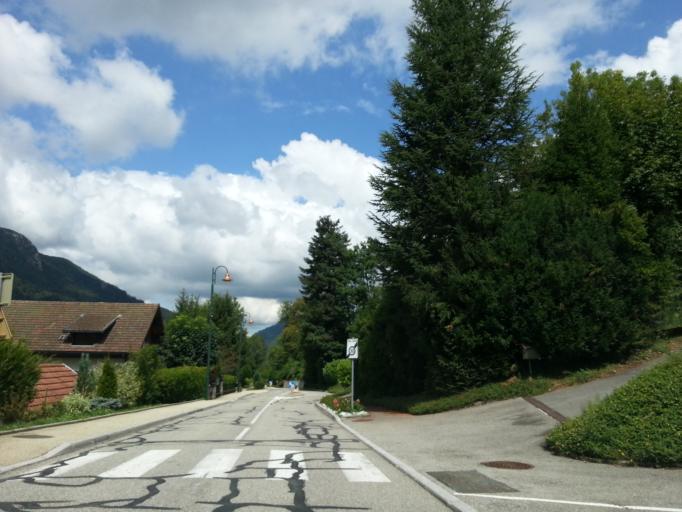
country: FR
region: Rhone-Alpes
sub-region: Departement de la Haute-Savoie
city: Menthon-Saint-Bernard
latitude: 45.8692
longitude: 6.2183
